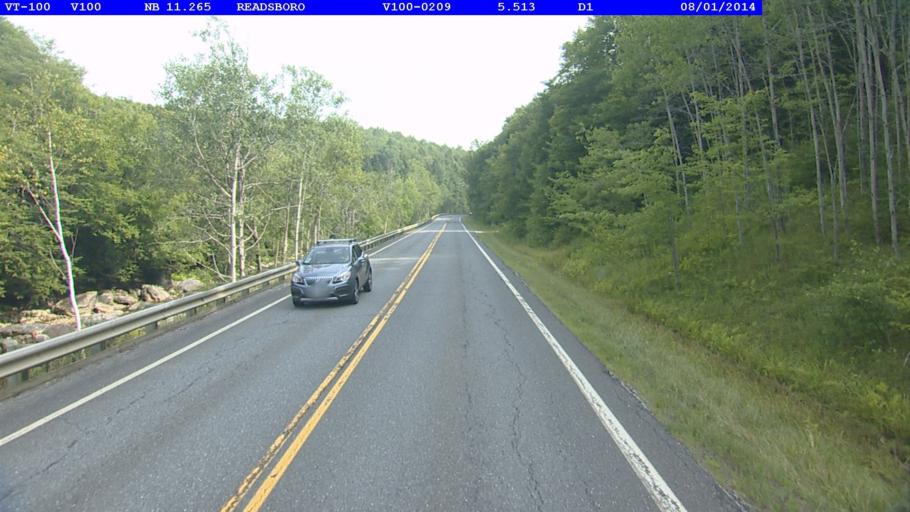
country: US
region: Massachusetts
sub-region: Berkshire County
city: North Adams
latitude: 42.7878
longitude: -72.9611
